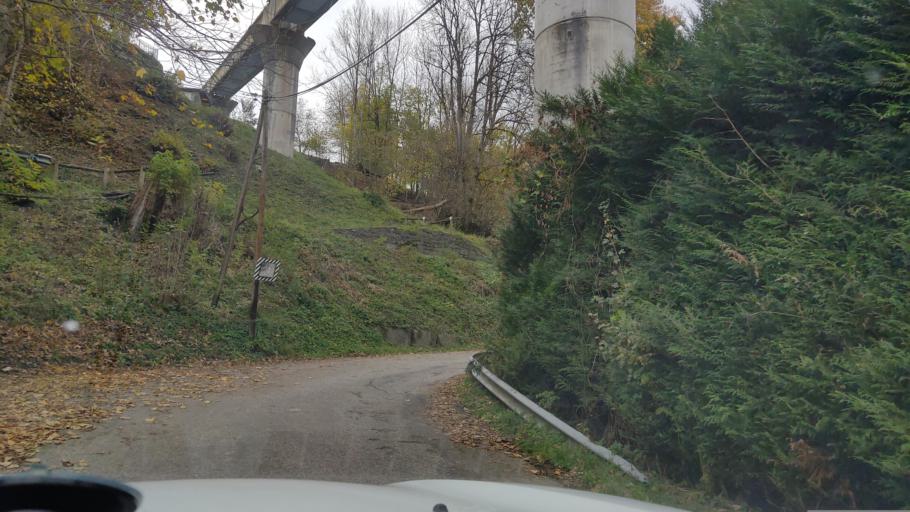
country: FR
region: Rhone-Alpes
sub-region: Departement de la Savoie
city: Bourg-Saint-Maurice
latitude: 45.6108
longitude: 6.7749
